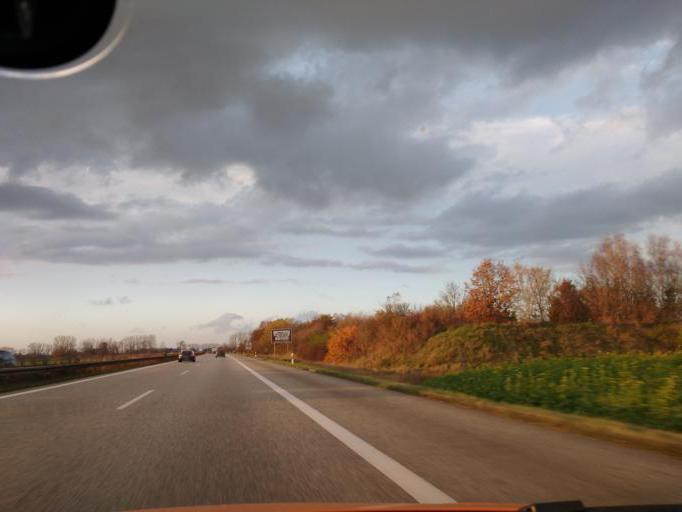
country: DE
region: Mecklenburg-Vorpommern
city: Neustadt-Glewe
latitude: 53.4055
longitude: 11.5711
